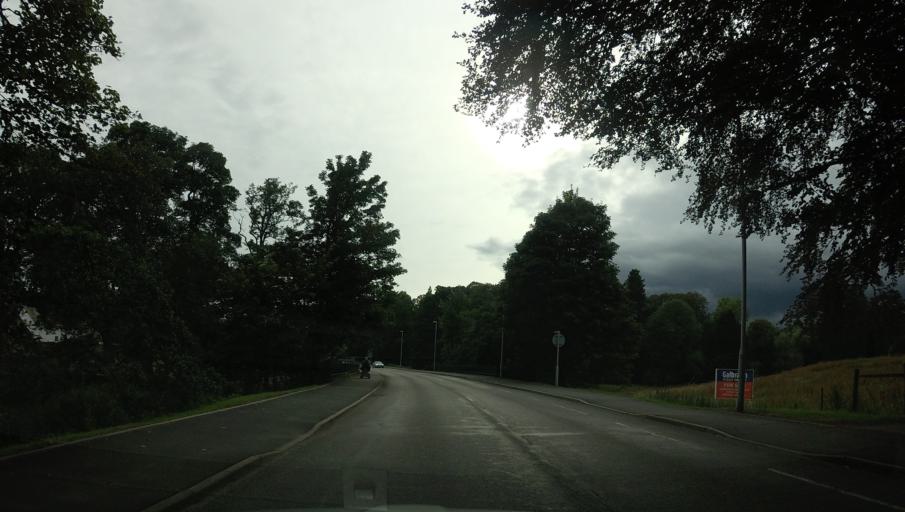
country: GB
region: Scotland
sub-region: Aberdeenshire
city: Aboyne
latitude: 57.0780
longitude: -2.7761
